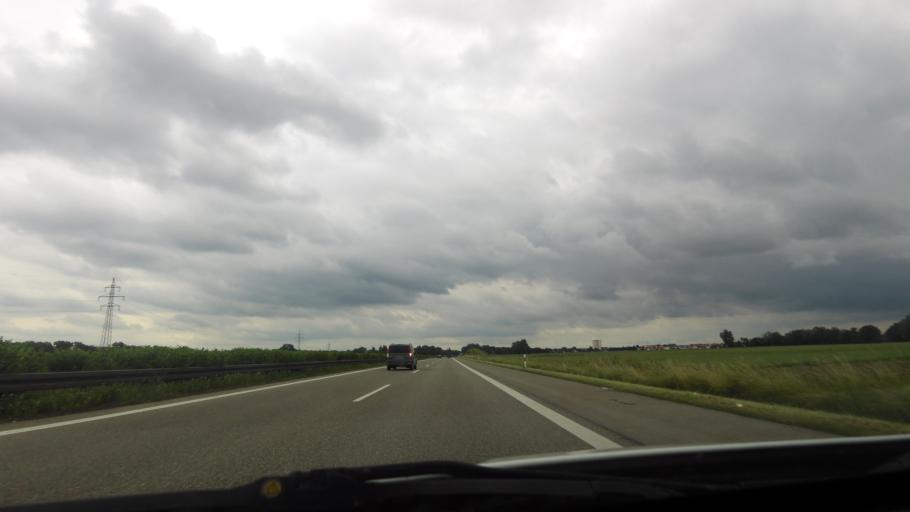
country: DE
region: Baden-Wuerttemberg
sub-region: Tuebingen Region
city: Dettingen an der Iller
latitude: 48.0937
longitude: 10.1343
